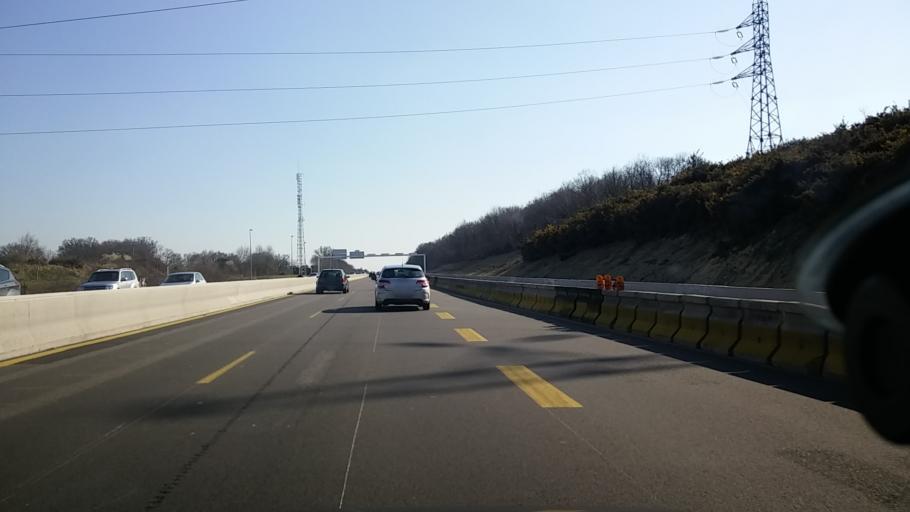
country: FR
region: Centre
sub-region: Departement du Loir-et-Cher
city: Theillay
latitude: 47.2860
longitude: 2.0435
